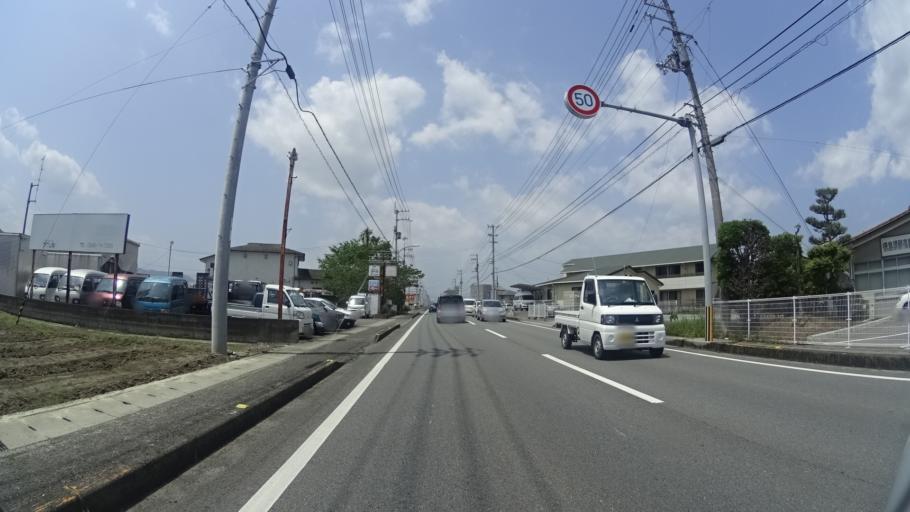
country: JP
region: Tokushima
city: Ishii
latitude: 34.0691
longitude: 134.4093
